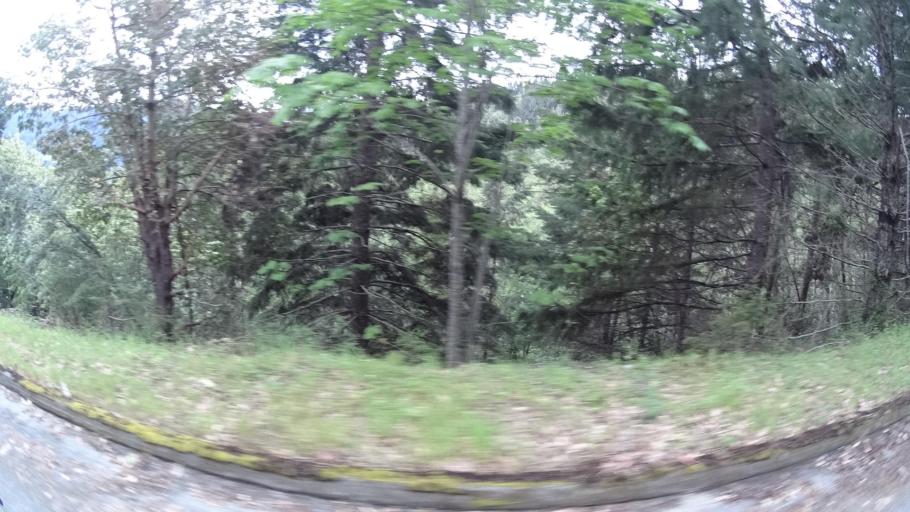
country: US
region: California
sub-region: Humboldt County
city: Blue Lake
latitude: 40.9362
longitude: -123.8491
